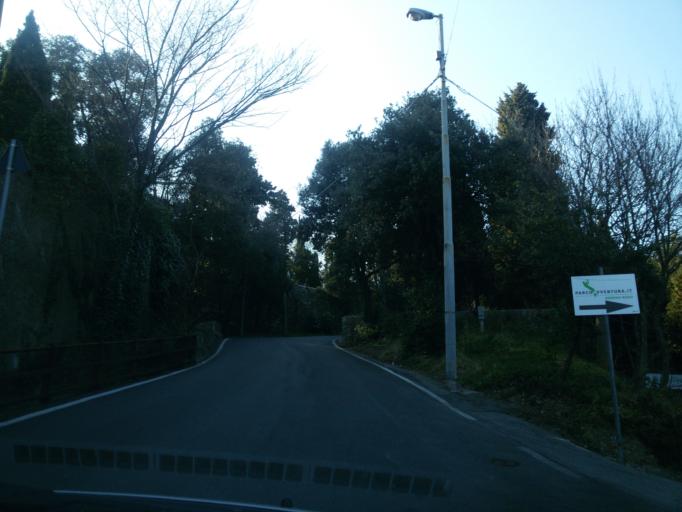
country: IT
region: Liguria
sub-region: Provincia di Genova
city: Genoa
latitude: 44.4215
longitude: 8.9401
